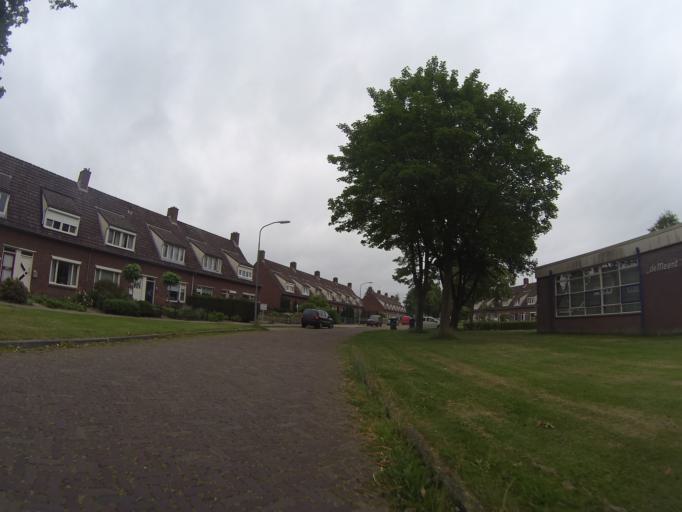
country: NL
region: Drenthe
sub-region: Gemeente Emmen
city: Emmer-Compascuum
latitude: 52.8128
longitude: 7.0534
